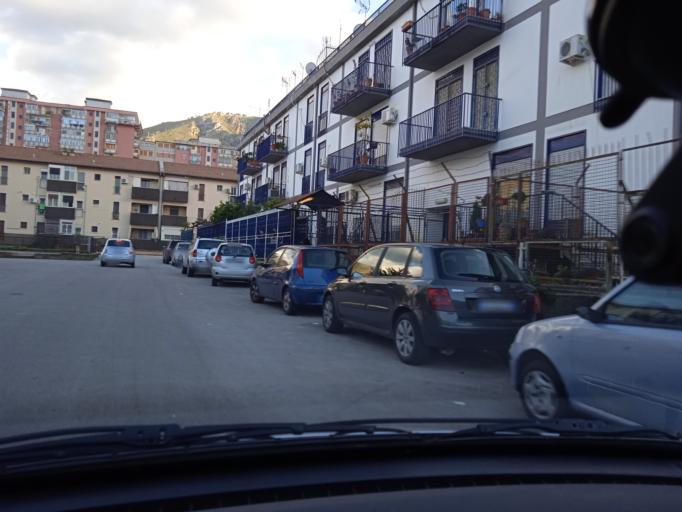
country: IT
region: Sicily
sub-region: Palermo
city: Villa Ciambra
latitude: 38.0855
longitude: 13.3588
